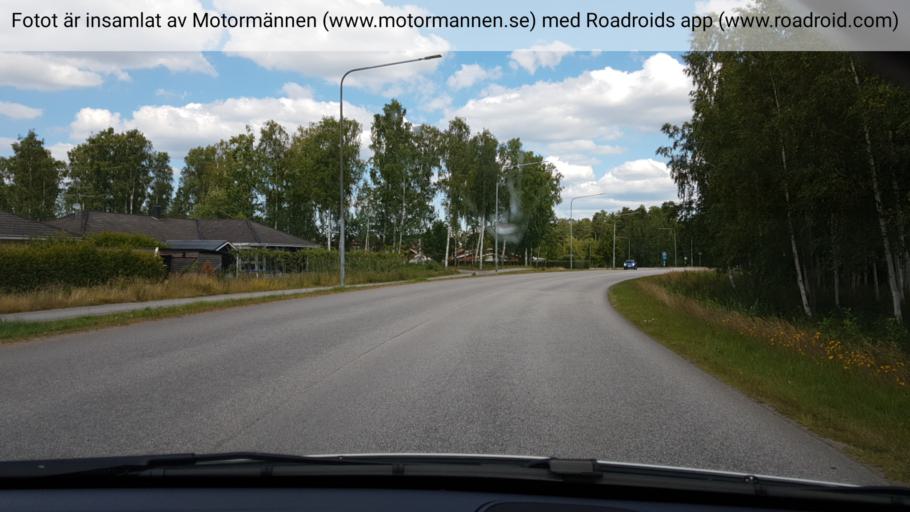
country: SE
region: Vaestra Goetaland
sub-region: Mariestads Kommun
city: Mariestad
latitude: 58.7125
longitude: 13.8614
